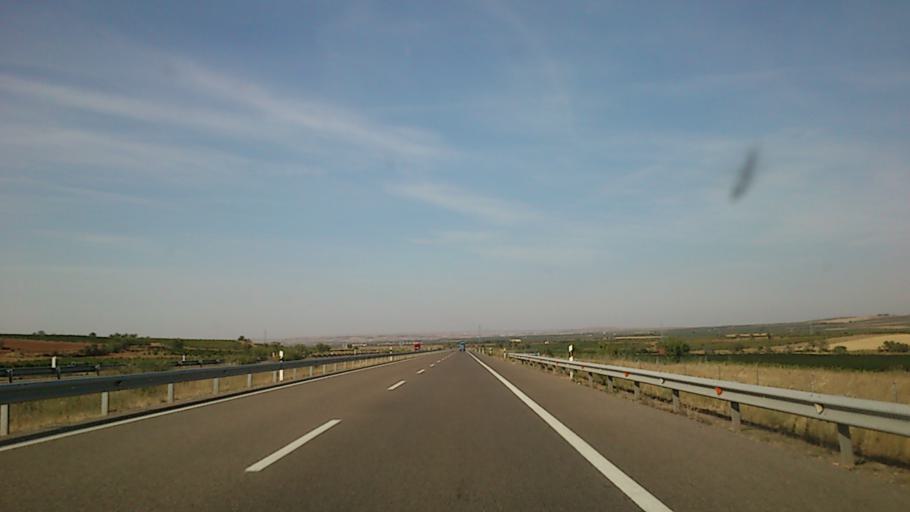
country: ES
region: Aragon
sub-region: Provincia de Zaragoza
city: Carinena
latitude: 41.3129
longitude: -1.2087
